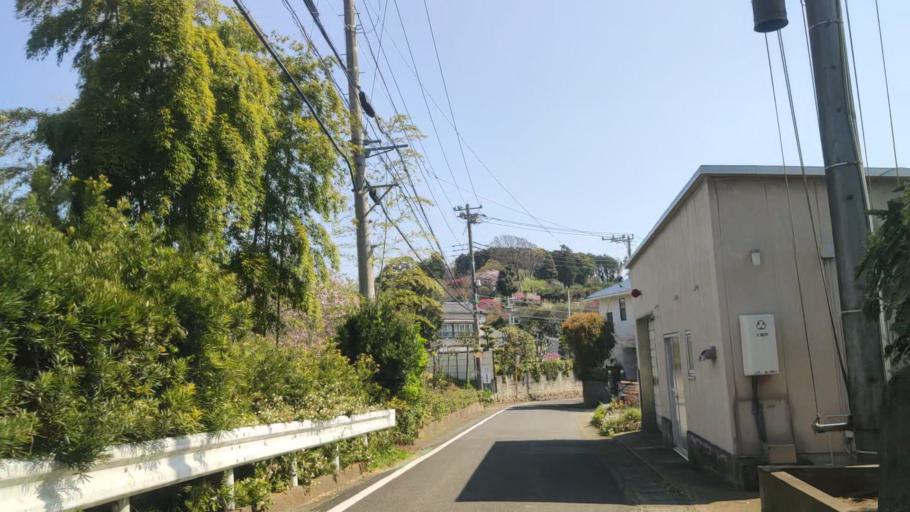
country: JP
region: Kanagawa
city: Ninomiya
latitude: 35.3266
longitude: 139.2570
